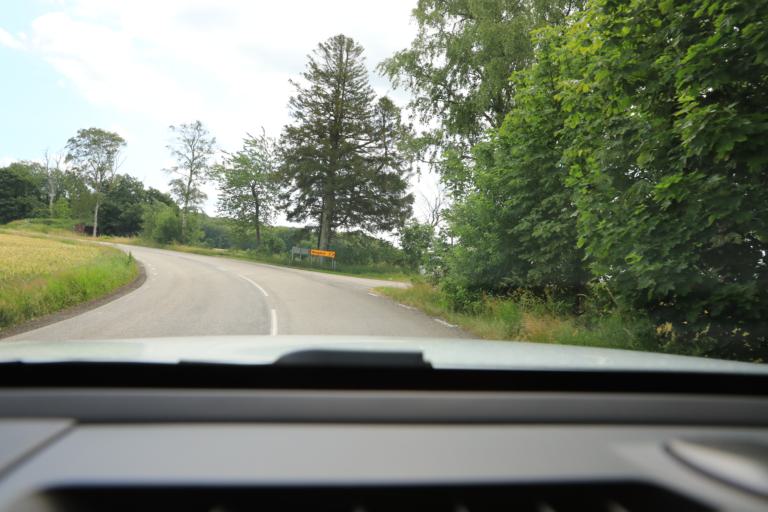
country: SE
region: Halland
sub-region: Varbergs Kommun
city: Tvaaker
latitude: 57.0319
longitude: 12.4464
